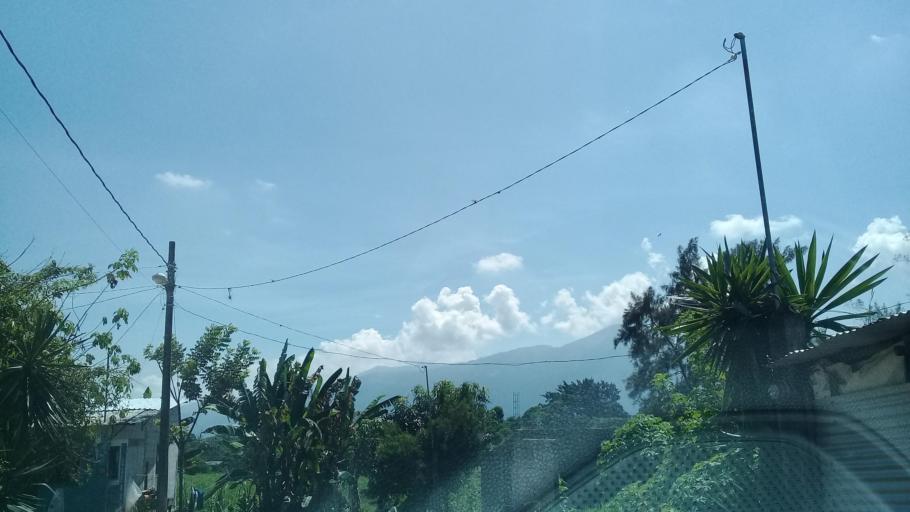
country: MX
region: Veracruz
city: Amatlan de los Reyes
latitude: 18.8378
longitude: -96.9146
